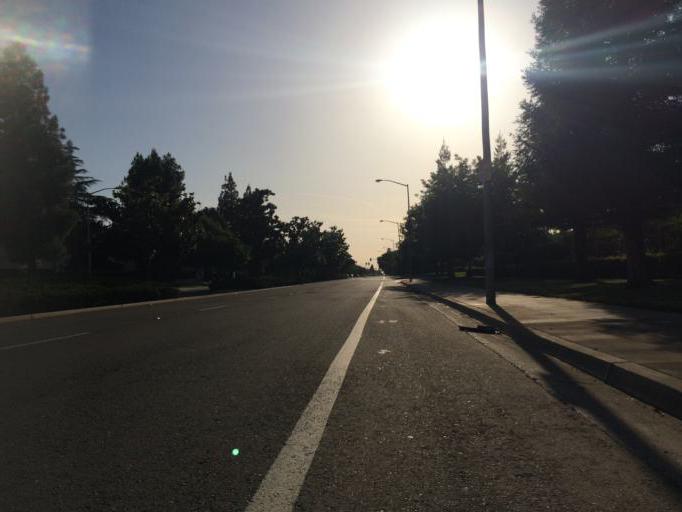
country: US
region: California
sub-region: Fresno County
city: Tarpey Village
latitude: 36.7723
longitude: -119.7291
